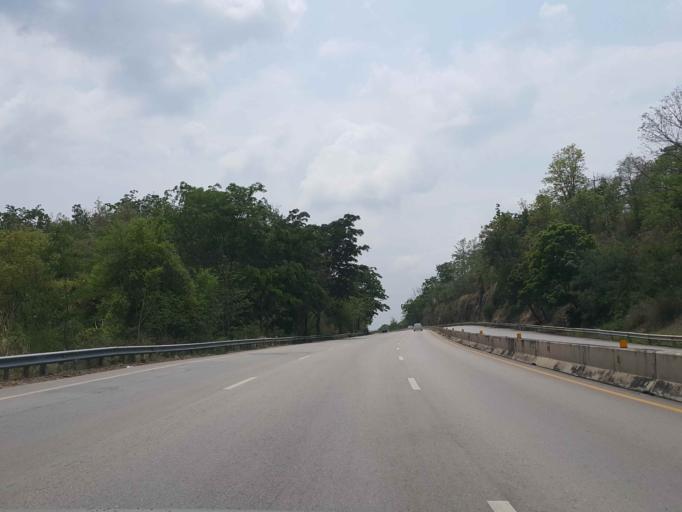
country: TH
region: Lampang
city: Soem Ngam
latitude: 18.0448
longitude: 99.3826
